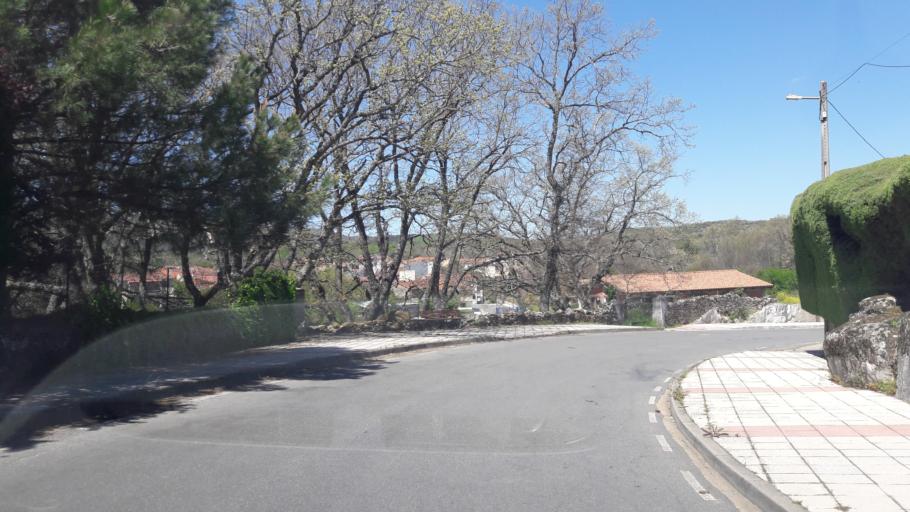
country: ES
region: Castille and Leon
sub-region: Provincia de Salamanca
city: Linares de Riofrio
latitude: 40.5827
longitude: -5.9158
